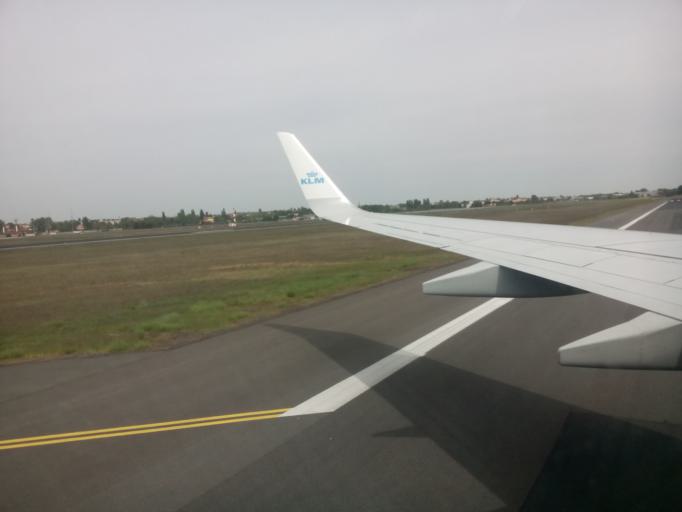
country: DE
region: Berlin
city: Tegel
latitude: 52.5592
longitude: 13.3009
